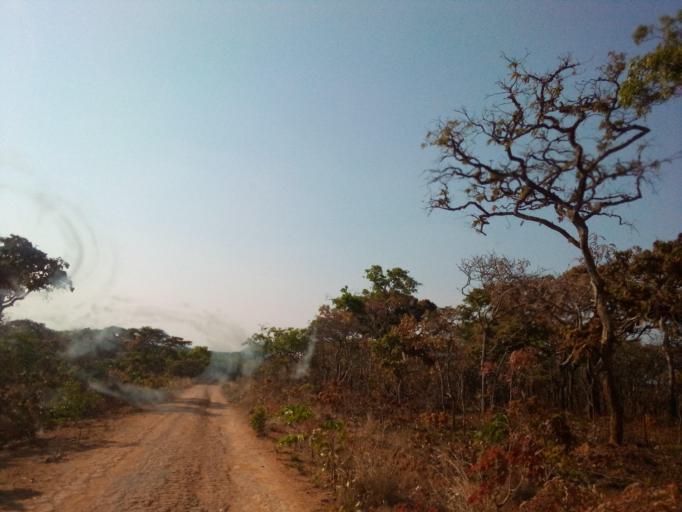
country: ZM
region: Northern
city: Mpika
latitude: -12.2142
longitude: 31.4377
